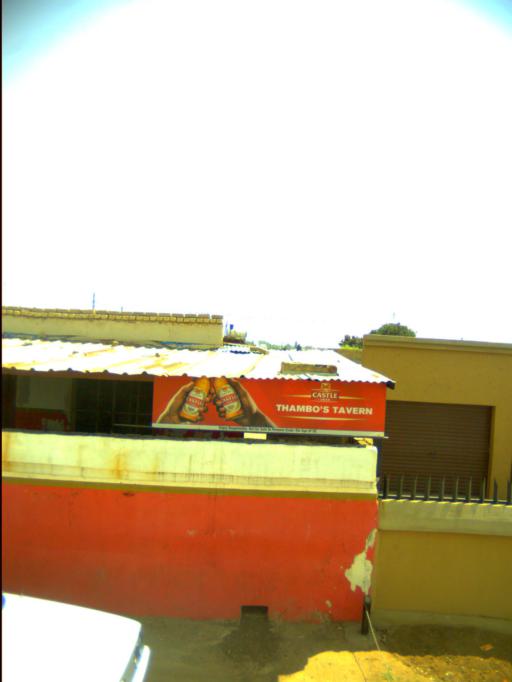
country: ZA
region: Mpumalanga
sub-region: Nkangala District Municipality
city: Delmas
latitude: -26.1425
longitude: 28.6916
